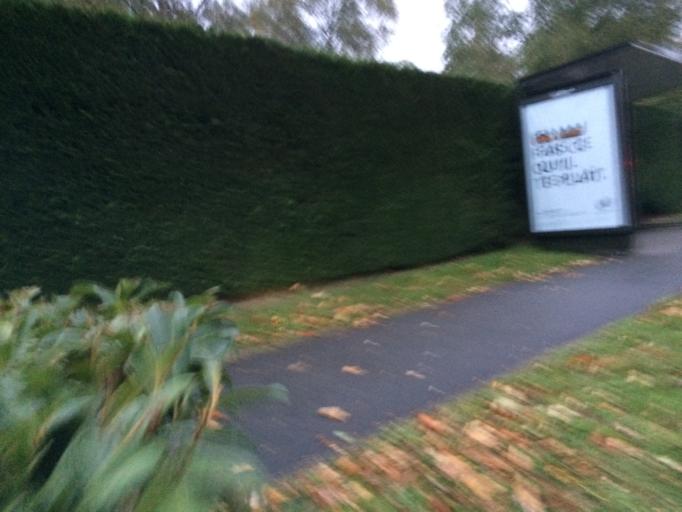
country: FR
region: Ile-de-France
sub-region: Departement de l'Essonne
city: Orsay
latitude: 48.6840
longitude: 2.1939
